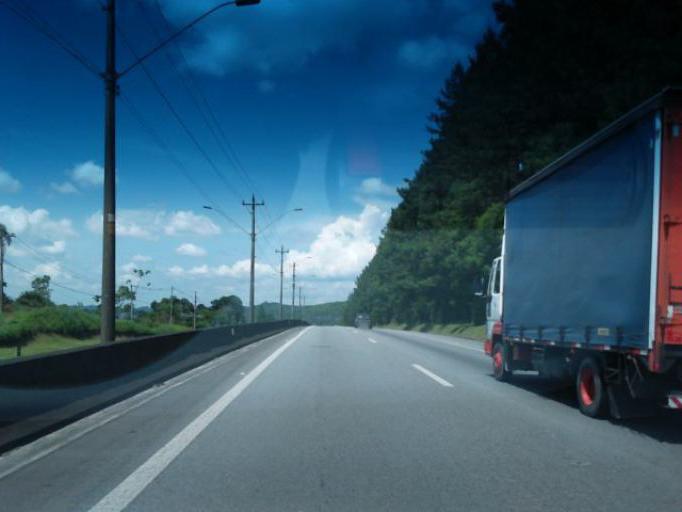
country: BR
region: Sao Paulo
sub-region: Sao Lourenco Da Serra
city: Sao Lourenco da Serra
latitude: -23.8710
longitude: -46.9603
